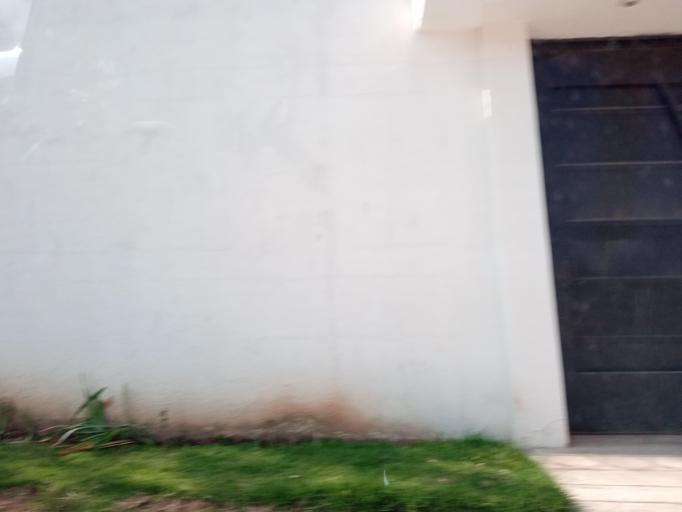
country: GT
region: Quetzaltenango
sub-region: Municipio de La Esperanza
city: La Esperanza
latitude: 14.8493
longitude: -91.5450
